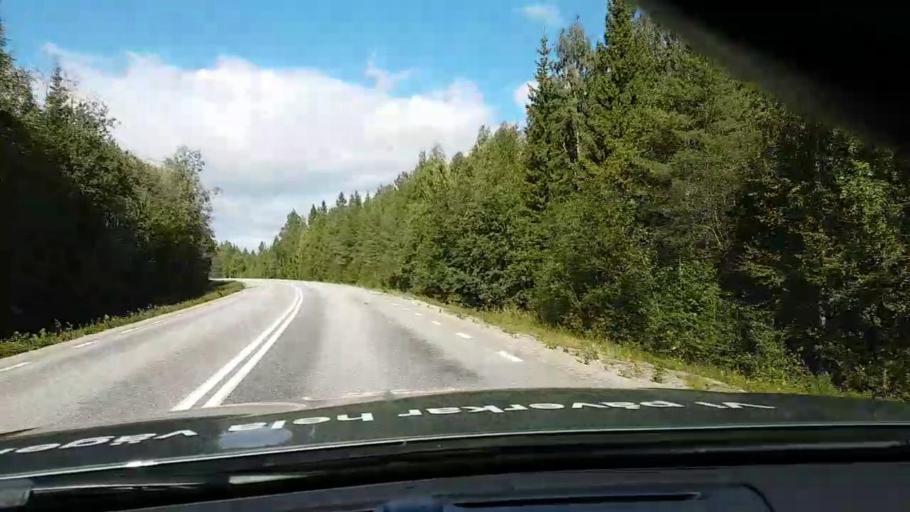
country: SE
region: Vaesternorrland
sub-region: OErnskoeldsviks Kommun
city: Bredbyn
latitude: 63.6307
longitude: 17.9109
